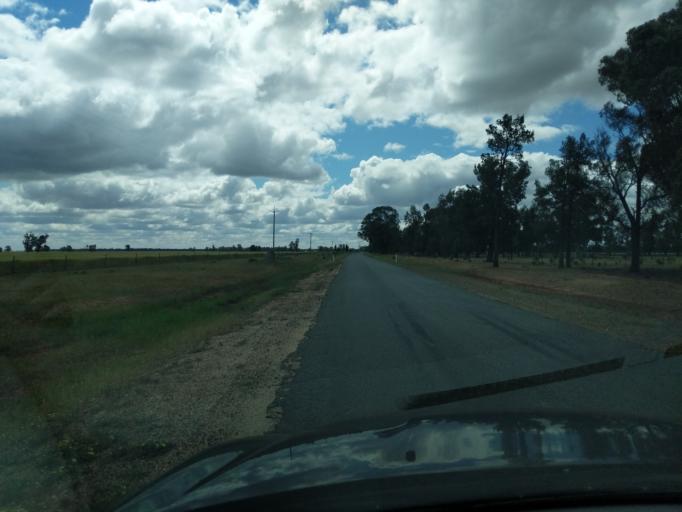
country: AU
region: New South Wales
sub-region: Coolamon
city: Coolamon
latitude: -34.8650
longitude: 146.8970
